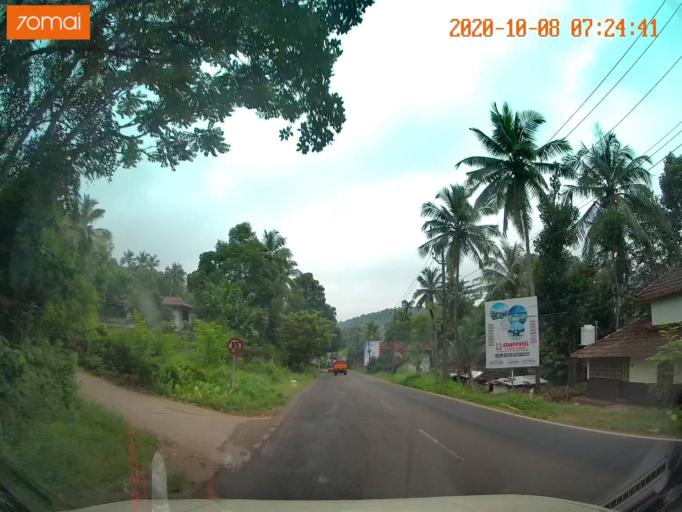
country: IN
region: Kerala
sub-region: Malappuram
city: Tirur
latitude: 10.8698
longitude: 76.0545
